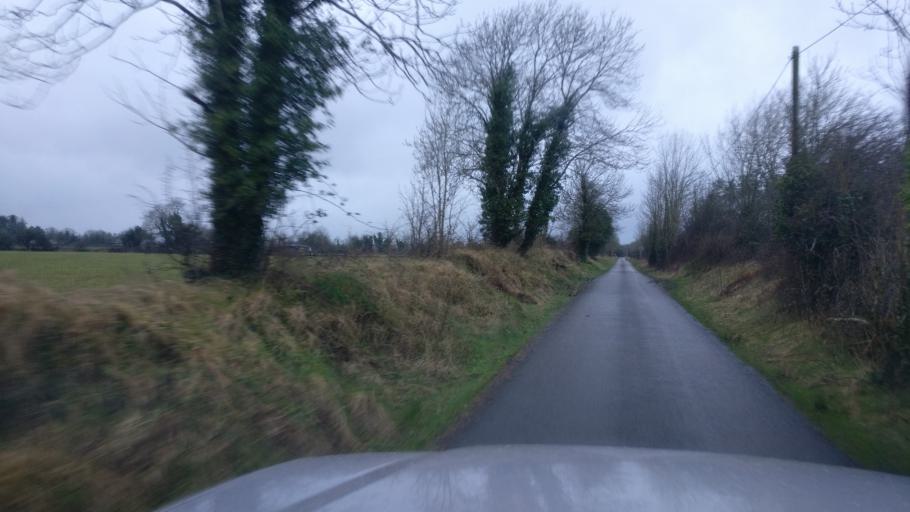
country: IE
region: Connaught
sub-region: County Galway
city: Ballinasloe
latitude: 53.2755
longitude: -8.3352
